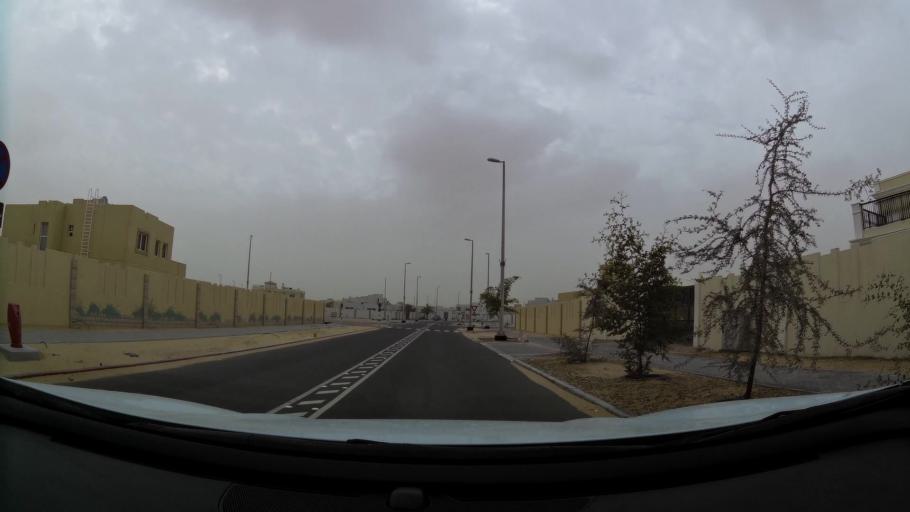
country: AE
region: Abu Dhabi
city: Abu Dhabi
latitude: 24.4380
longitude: 54.7343
